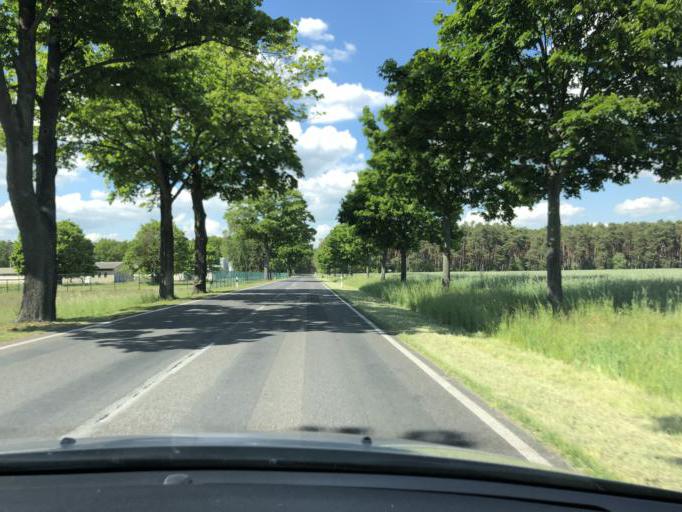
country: DE
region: Brandenburg
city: Storkow
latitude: 52.2936
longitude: 13.9045
